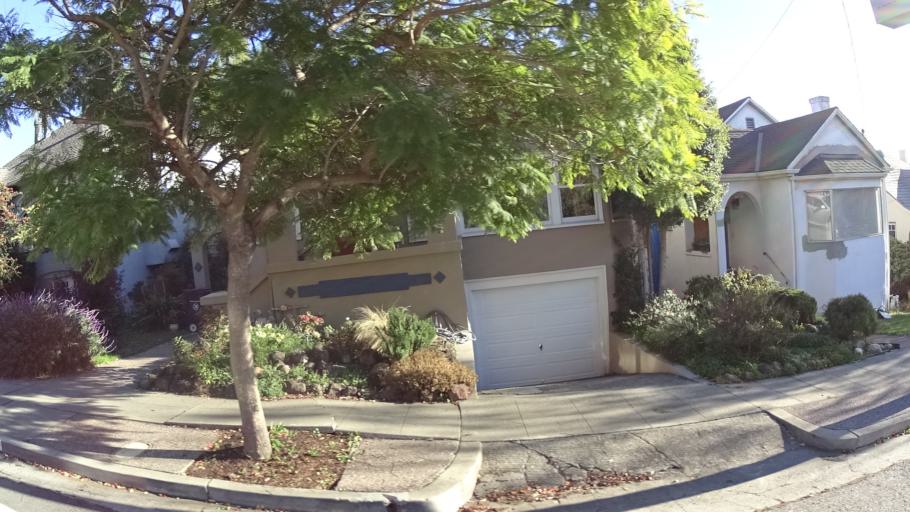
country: US
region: California
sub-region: Alameda County
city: Piedmont
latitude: 37.8115
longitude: -122.2171
